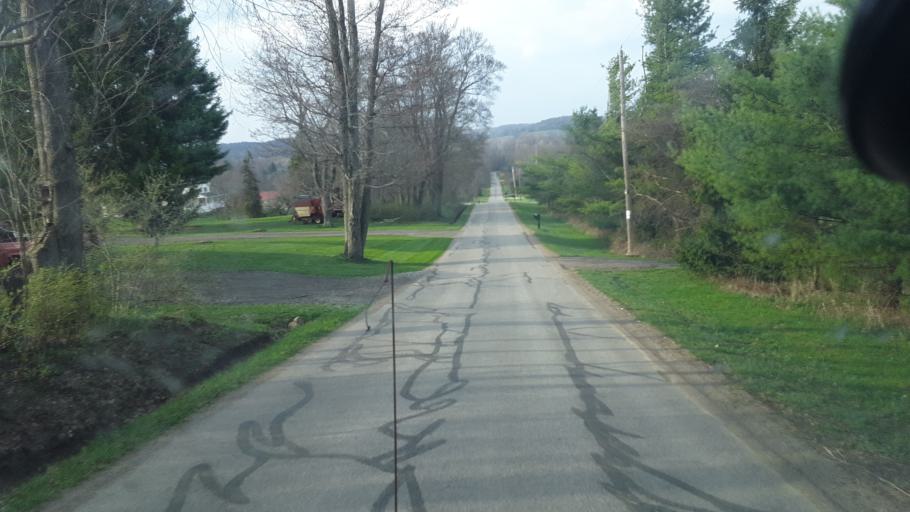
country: US
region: Ohio
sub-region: Richland County
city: Lincoln Heights
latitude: 40.7206
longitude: -82.4268
